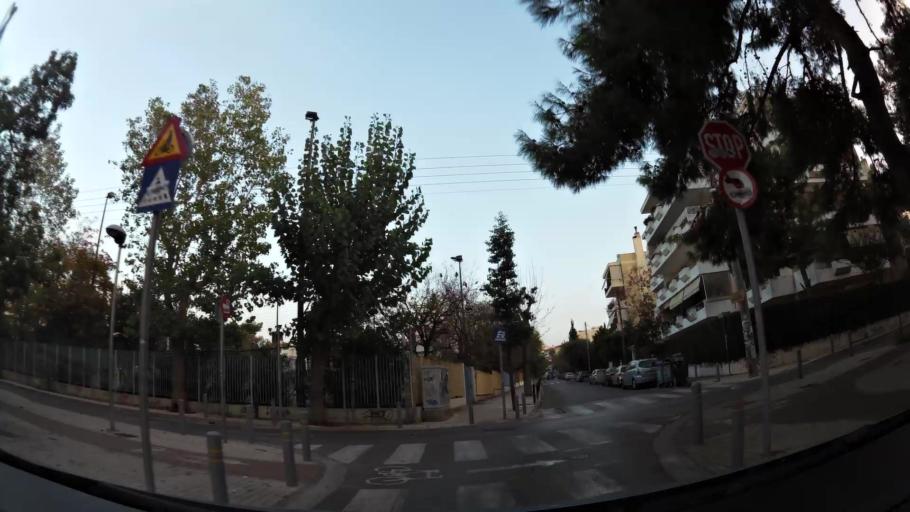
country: GR
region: Attica
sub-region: Nomarchia Athinas
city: Agia Paraskevi
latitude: 38.0173
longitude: 23.8325
